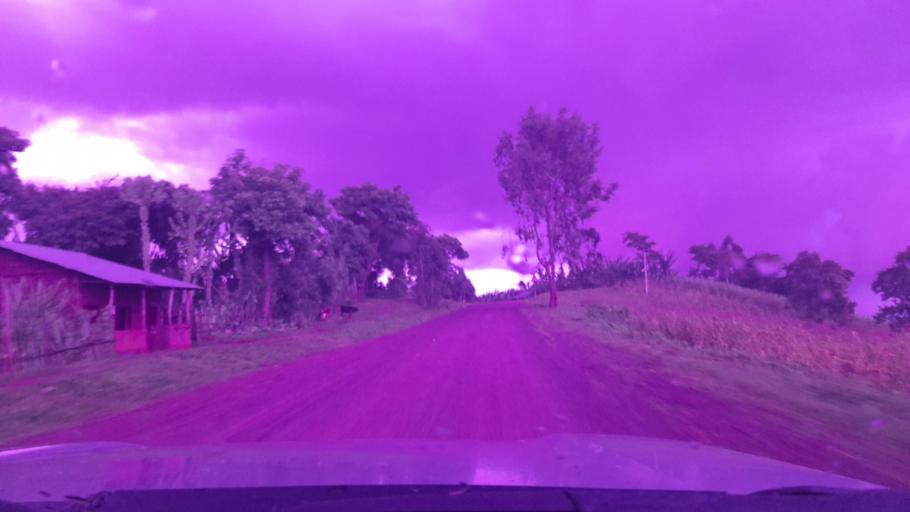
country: ET
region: Southern Nations, Nationalities, and People's Region
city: Mizan Teferi
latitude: 6.9127
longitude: 35.8425
